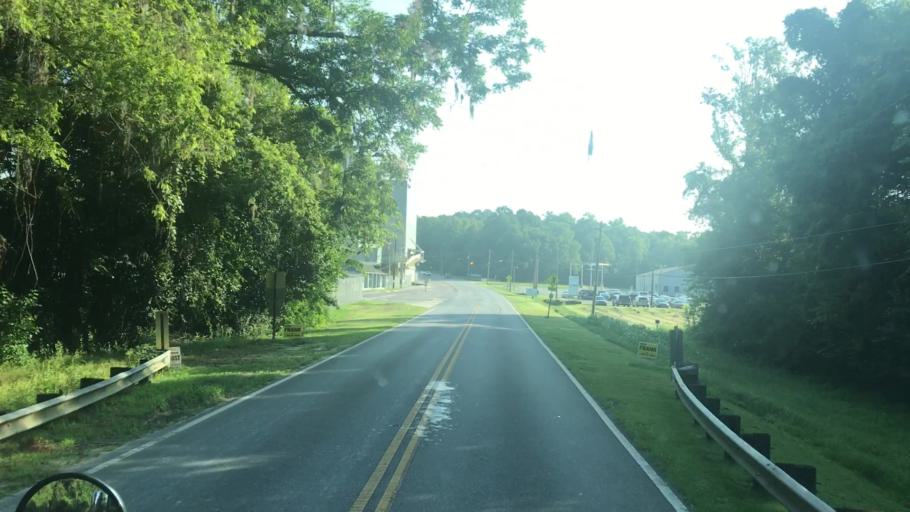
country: US
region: Florida
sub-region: Gadsden County
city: Quincy
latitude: 30.5984
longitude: -84.5739
